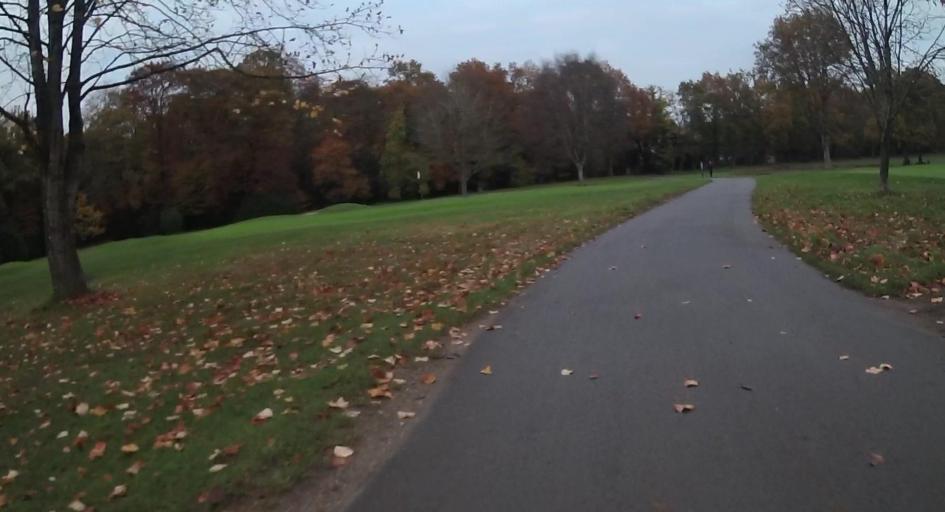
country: GB
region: England
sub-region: Bracknell Forest
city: Crowthorne
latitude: 51.3733
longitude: -0.8177
